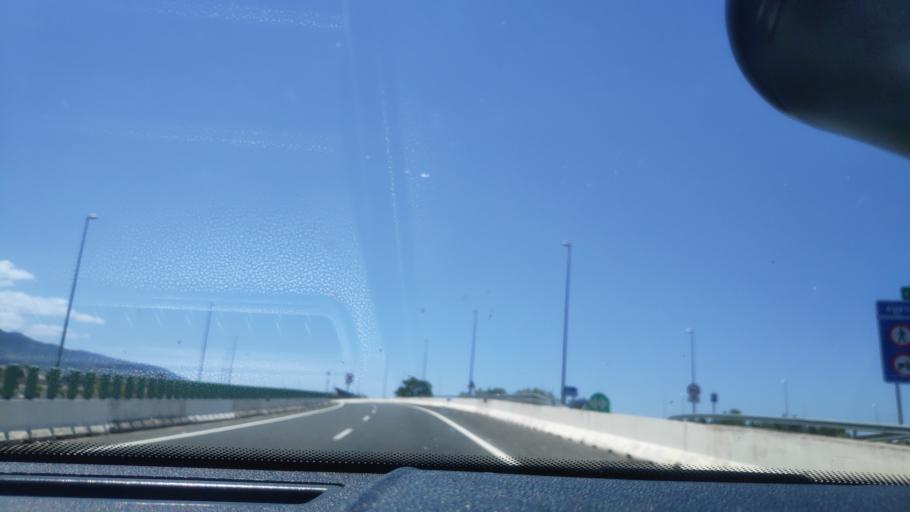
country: ES
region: Andalusia
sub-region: Provincia de Jaen
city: Jaen
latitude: 37.8193
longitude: -3.7623
